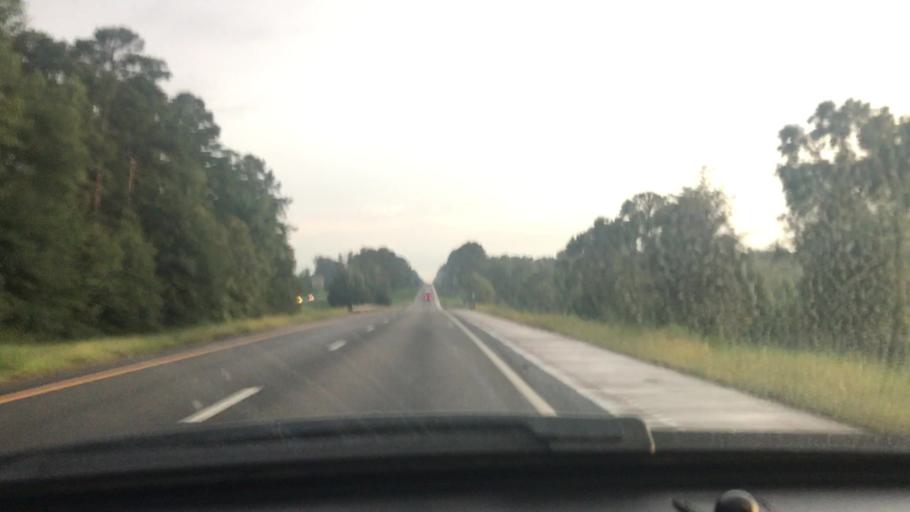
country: US
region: Mississippi
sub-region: Pike County
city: Magnolia
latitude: 31.1013
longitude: -90.4874
